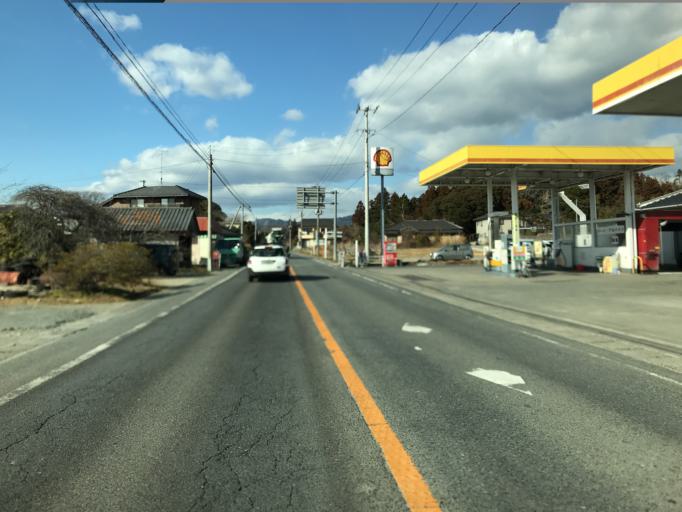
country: JP
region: Fukushima
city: Iwaki
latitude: 37.1088
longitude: 140.8746
